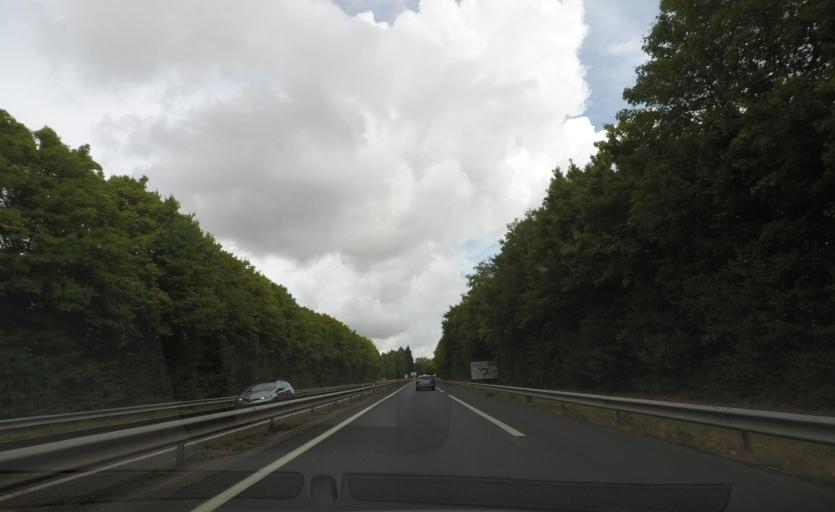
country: FR
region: Pays de la Loire
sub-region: Departement de Maine-et-Loire
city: Pellouailles-les-Vignes
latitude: 47.5224
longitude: -0.4276
